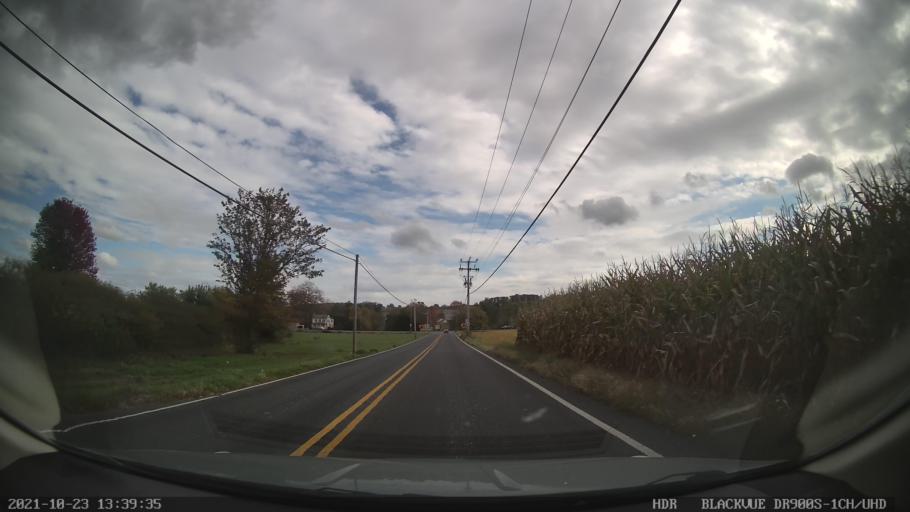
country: US
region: Pennsylvania
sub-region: Berks County
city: Bally
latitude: 40.4251
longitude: -75.5712
